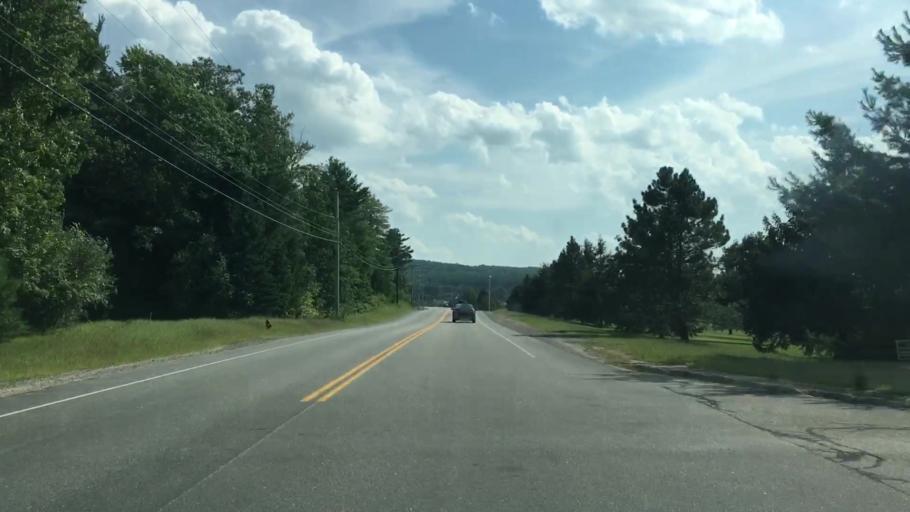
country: US
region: New Hampshire
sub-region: Belknap County
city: Tilton
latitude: 43.4625
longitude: -71.5654
